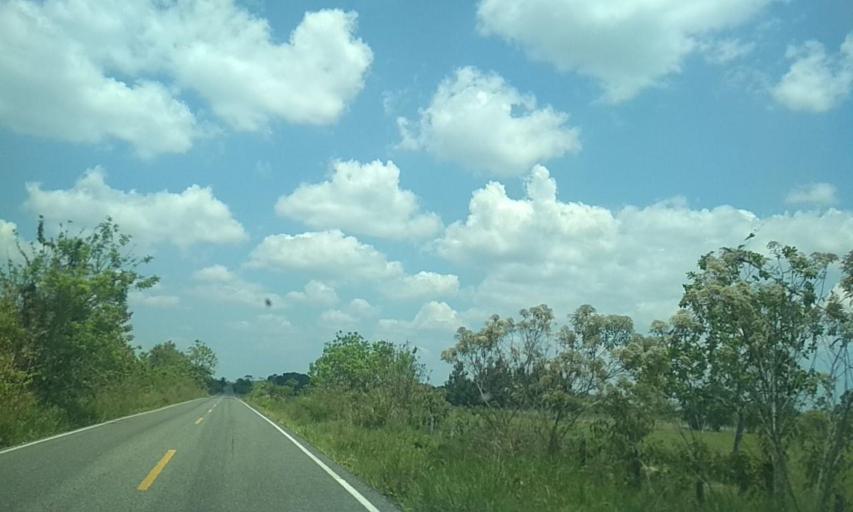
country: MX
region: Tabasco
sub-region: Huimanguillo
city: Huapacal 1ra. Seccion
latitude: 17.7535
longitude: -93.7419
